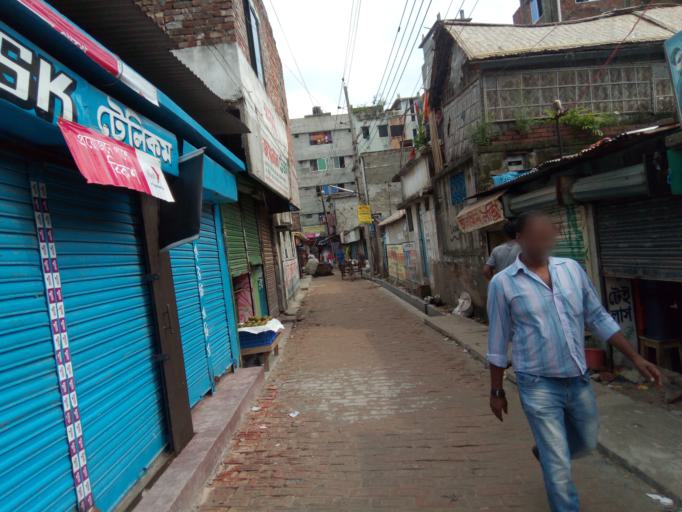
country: BD
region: Dhaka
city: Azimpur
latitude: 23.7378
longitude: 90.3633
